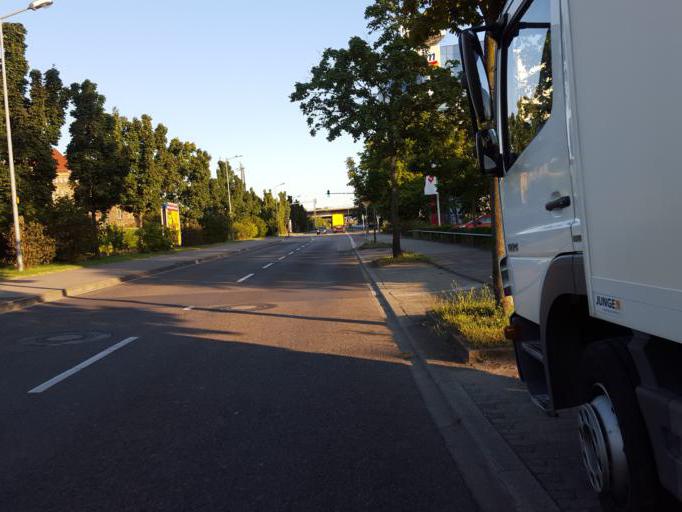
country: DE
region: Baden-Wuerttemberg
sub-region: Karlsruhe Region
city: Karlsruhe
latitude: 49.0113
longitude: 8.3528
